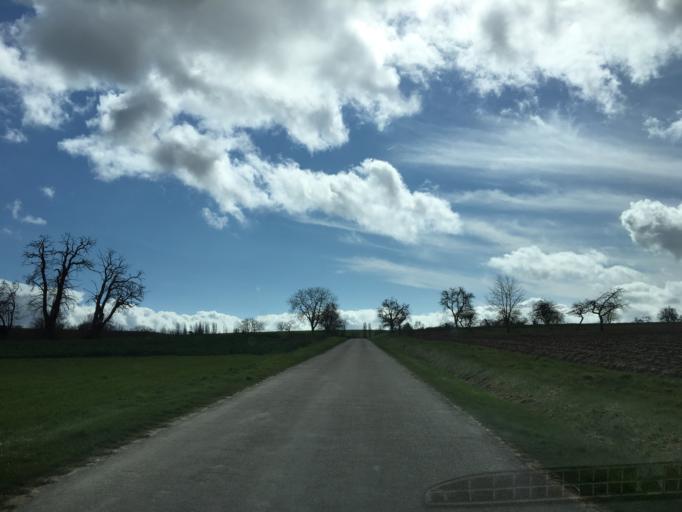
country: FR
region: Bourgogne
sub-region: Departement de l'Yonne
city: Pourrain
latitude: 47.7880
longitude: 3.4052
